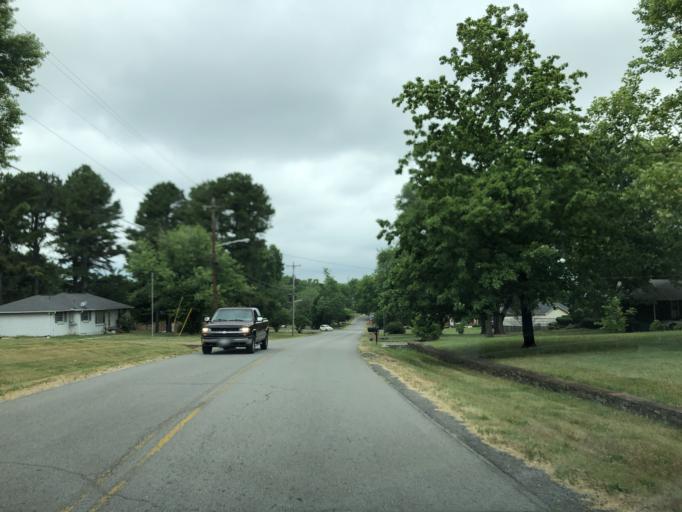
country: US
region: Tennessee
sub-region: Davidson County
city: Goodlettsville
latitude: 36.2819
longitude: -86.7267
